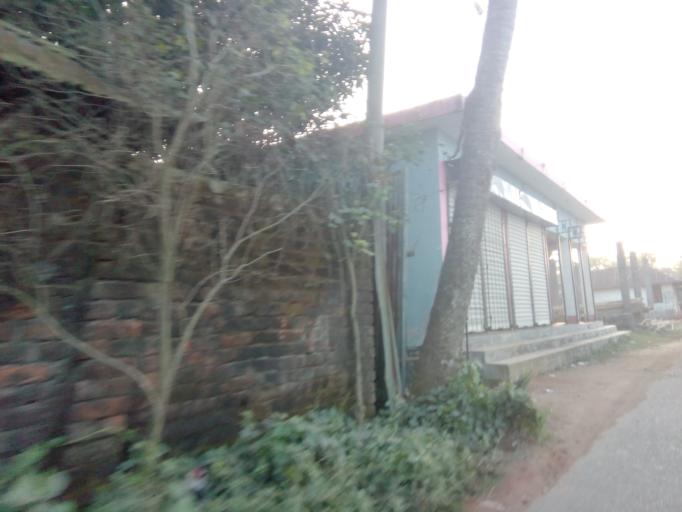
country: BD
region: Chittagong
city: Comilla
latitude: 23.4056
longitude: 91.1739
